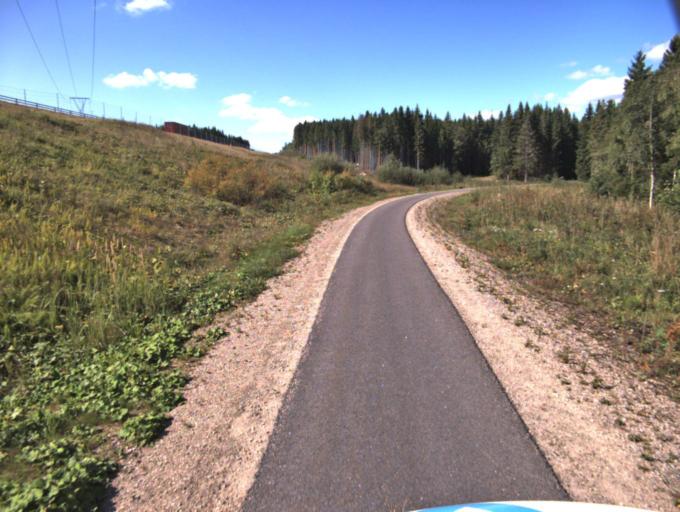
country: SE
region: Vaestra Goetaland
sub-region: Ulricehamns Kommun
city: Ulricehamn
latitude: 57.8169
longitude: 13.3496
